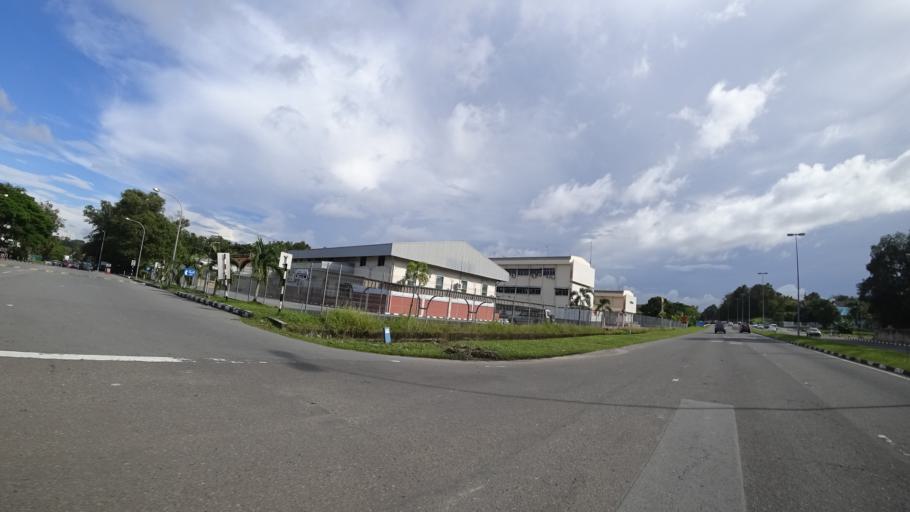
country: BN
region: Brunei and Muara
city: Bandar Seri Begawan
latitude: 4.8929
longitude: 114.8987
